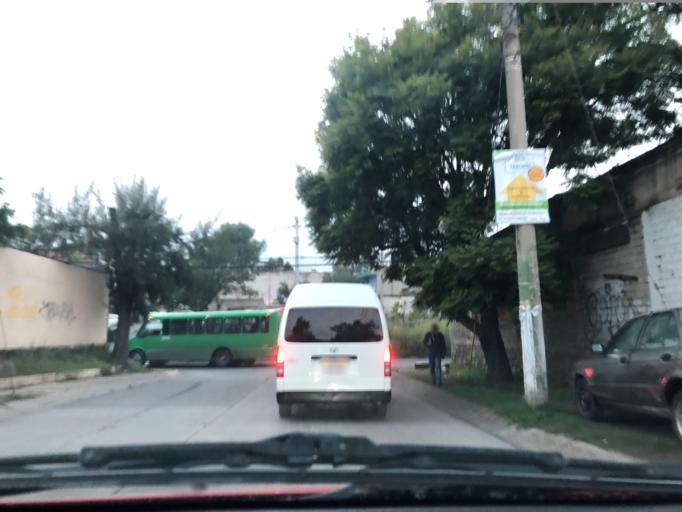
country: MX
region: Jalisco
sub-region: San Pedro Tlaquepaque
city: Paseo del Prado
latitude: 20.6144
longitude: -103.3937
